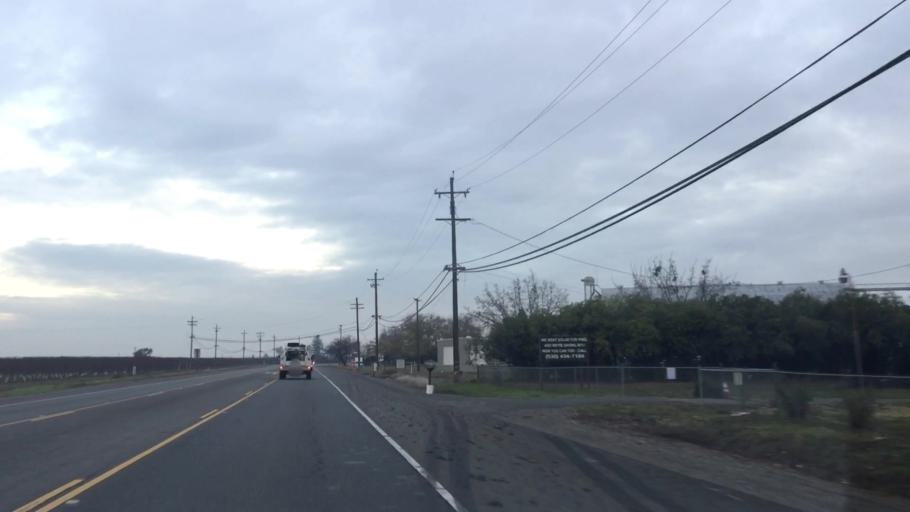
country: US
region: California
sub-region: Yuba County
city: Marysville
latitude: 39.2157
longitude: -121.5999
